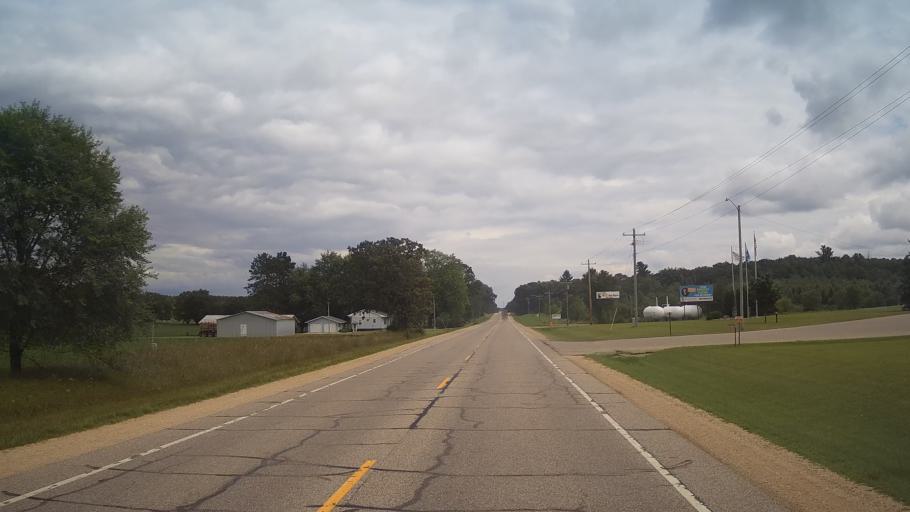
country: US
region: Wisconsin
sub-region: Waushara County
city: Wautoma
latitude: 44.0684
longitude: -89.3266
